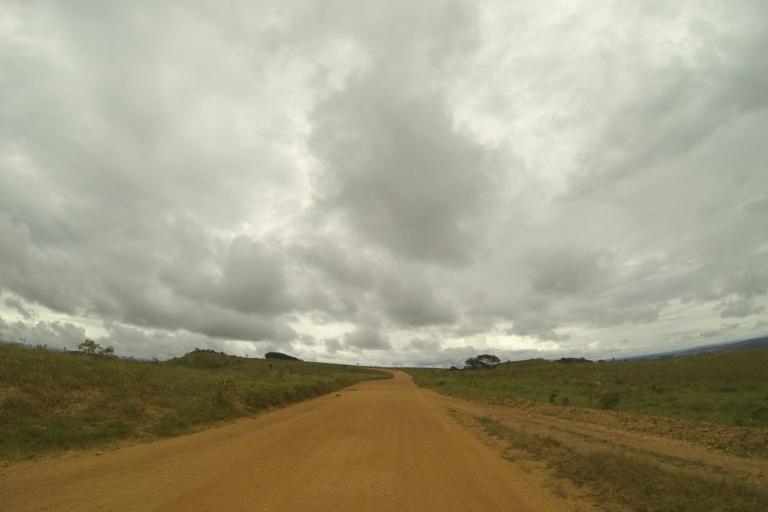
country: BR
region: Minas Gerais
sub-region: Ibia
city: Ibia
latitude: -19.7425
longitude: -46.4744
